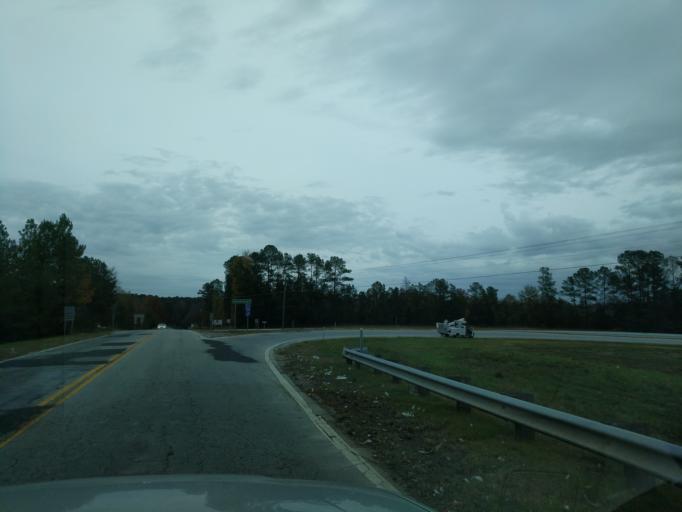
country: US
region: South Carolina
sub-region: Newberry County
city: Newberry
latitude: 34.3314
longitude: -81.6091
